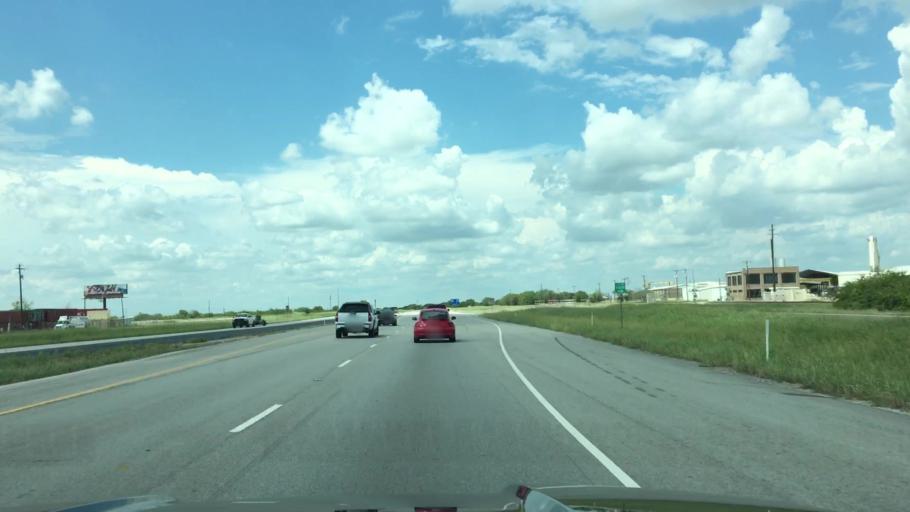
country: US
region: Texas
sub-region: Wise County
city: Rhome
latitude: 33.0346
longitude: -97.4515
